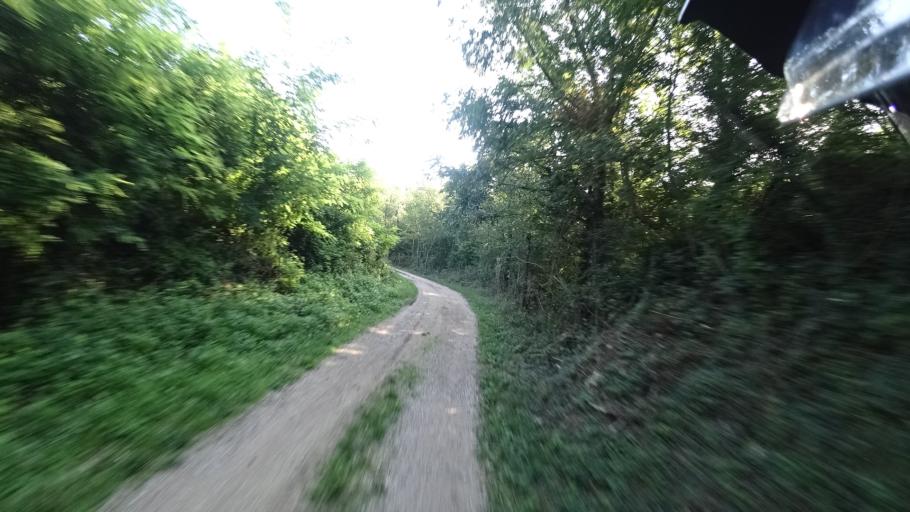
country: HR
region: Sibensko-Kniniska
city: Knin
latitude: 44.0703
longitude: 16.2044
